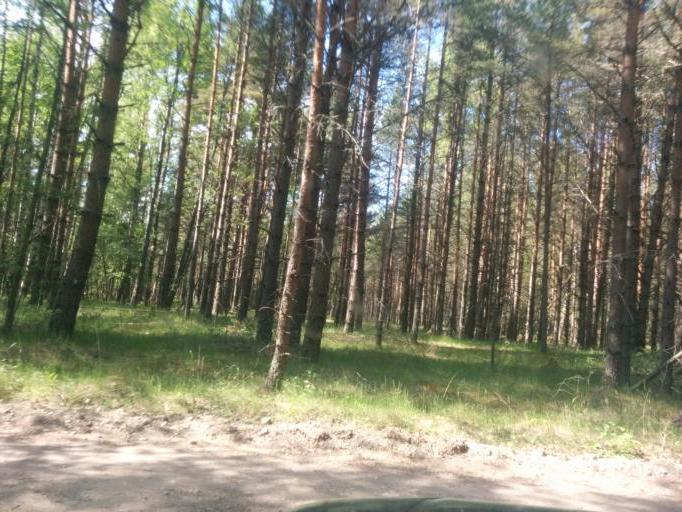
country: LV
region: Dundaga
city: Dundaga
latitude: 57.6243
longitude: 22.1055
